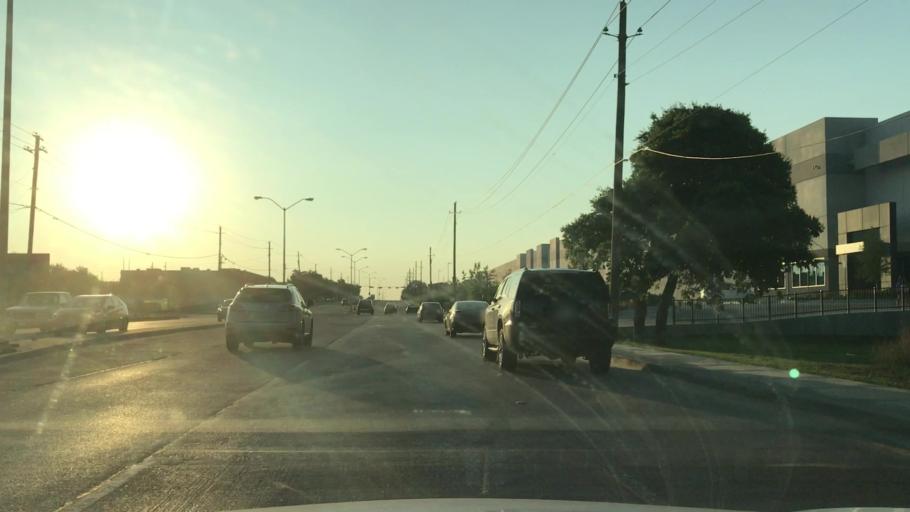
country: US
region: Texas
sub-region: Dallas County
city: Garland
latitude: 32.8945
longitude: -96.6979
